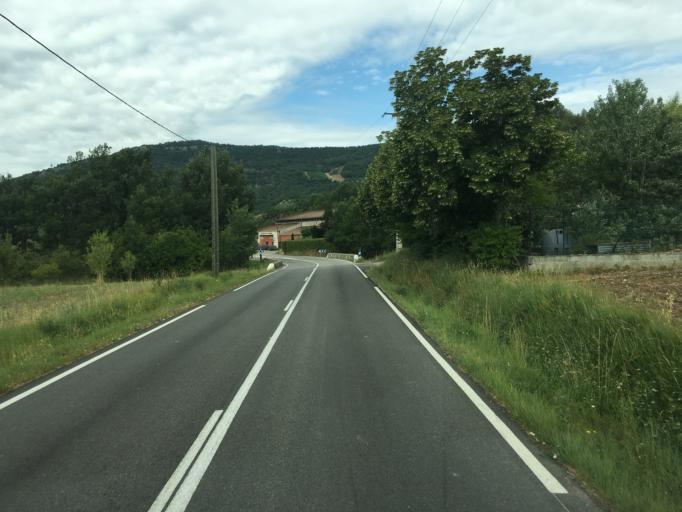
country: FR
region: Rhone-Alpes
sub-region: Departement de la Drome
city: Nyons
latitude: 44.3918
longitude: 5.2062
